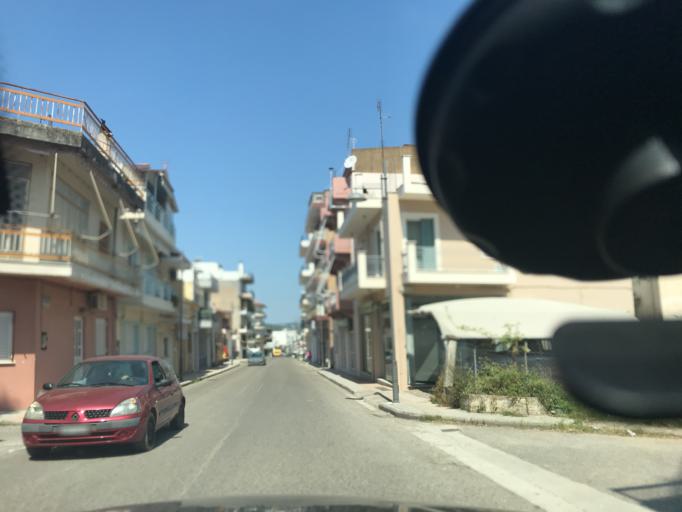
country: GR
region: West Greece
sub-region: Nomos Ileias
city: Pyrgos
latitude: 37.6748
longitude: 21.4425
